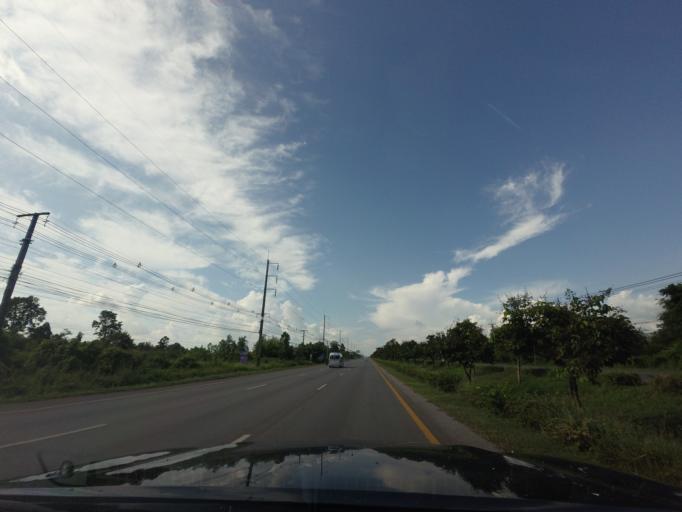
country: TH
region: Nong Khai
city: Nong Khai
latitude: 17.7887
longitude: 102.7639
